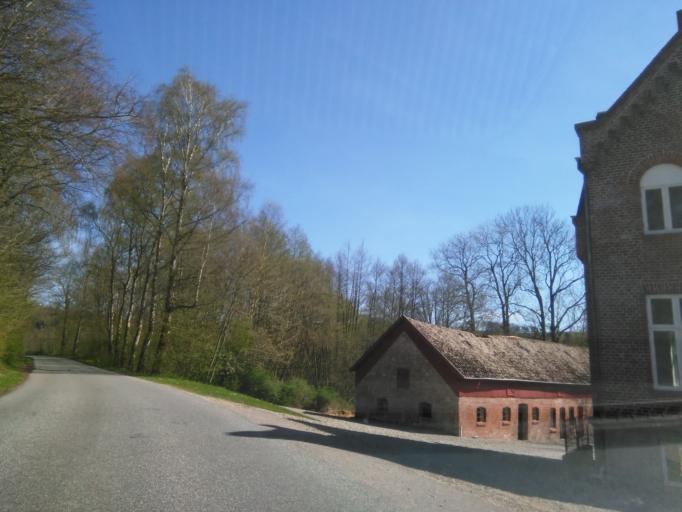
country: DK
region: Central Jutland
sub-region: Viborg Kommune
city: Viborg
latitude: 56.3673
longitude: 9.3246
